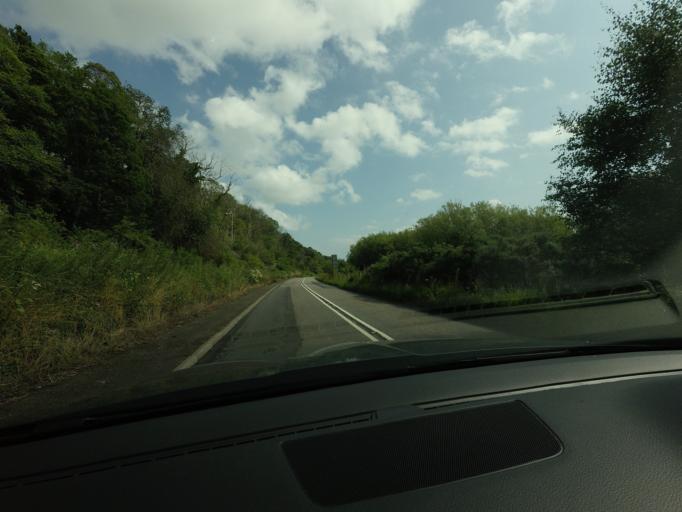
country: GB
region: Scotland
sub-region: Highland
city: Dingwall
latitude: 57.6060
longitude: -4.4178
